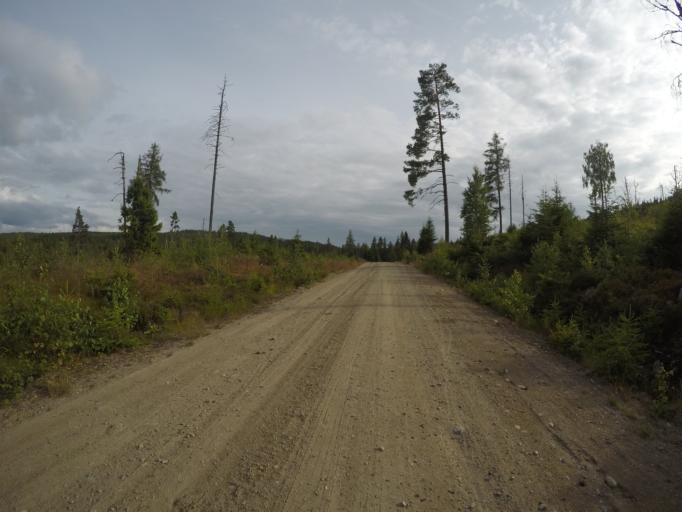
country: SE
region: Vaermland
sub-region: Filipstads Kommun
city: Lesjofors
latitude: 60.1999
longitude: 14.3184
